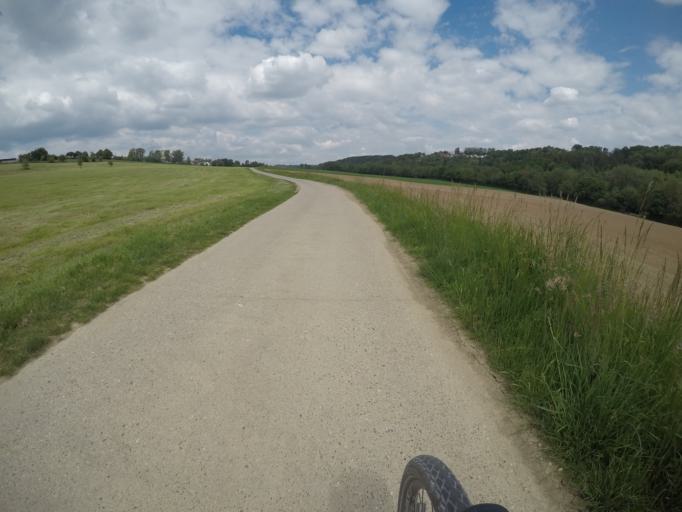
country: DE
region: Baden-Wuerttemberg
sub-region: Regierungsbezirk Stuttgart
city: Ostfildern
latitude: 48.7135
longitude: 9.2223
